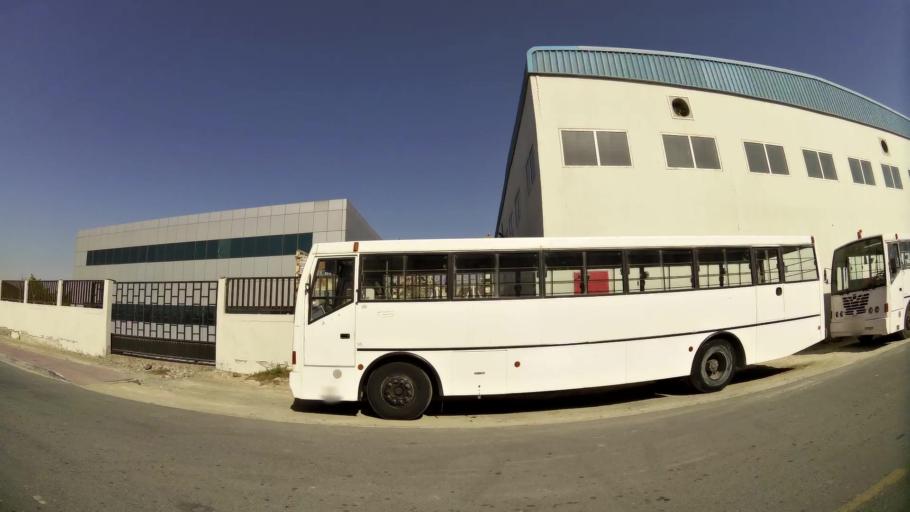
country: AE
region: Dubai
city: Dubai
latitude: 24.9909
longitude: 55.1076
